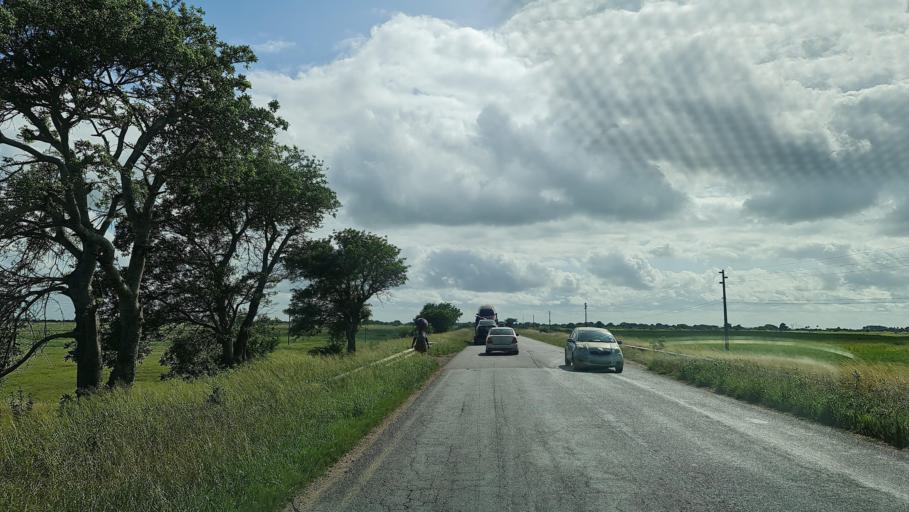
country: MZ
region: Gaza
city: Macia
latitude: -25.0963
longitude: 32.8306
